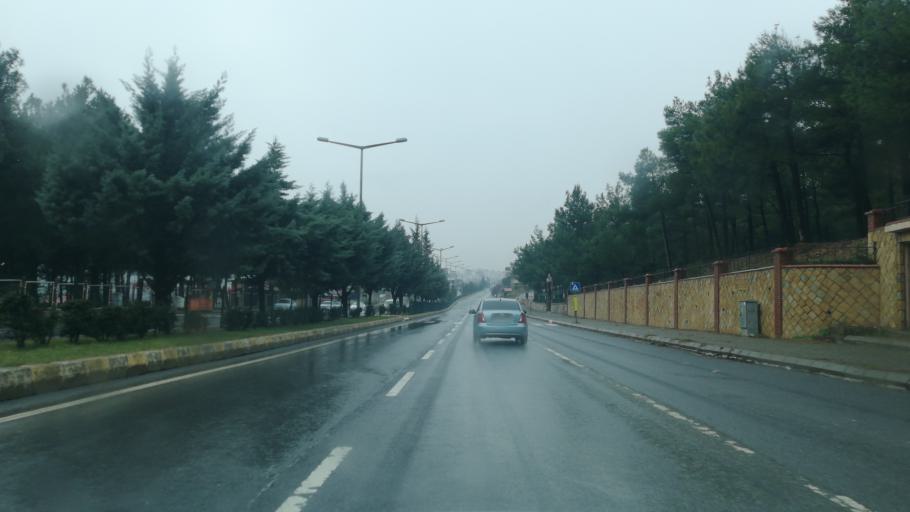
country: TR
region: Kahramanmaras
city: Kahramanmaras
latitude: 37.5986
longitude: 36.9211
